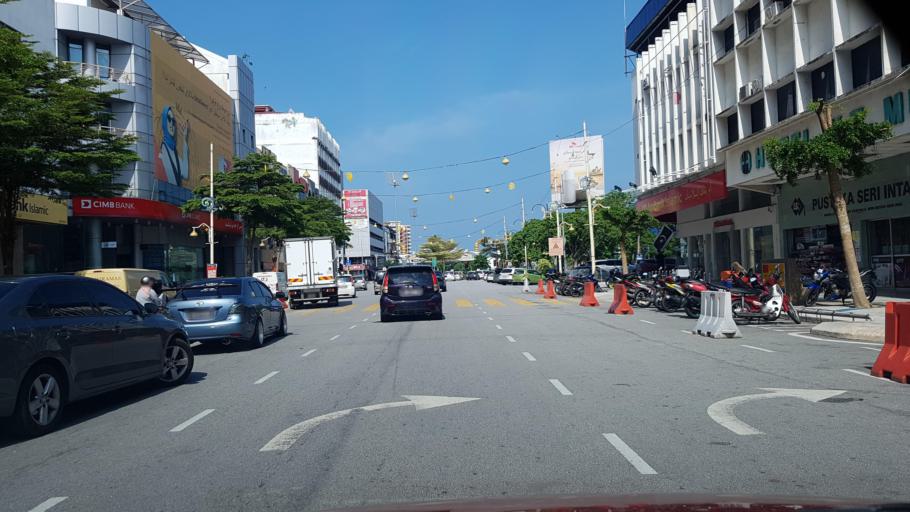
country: MY
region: Terengganu
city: Kuala Terengganu
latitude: 5.3299
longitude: 103.1367
